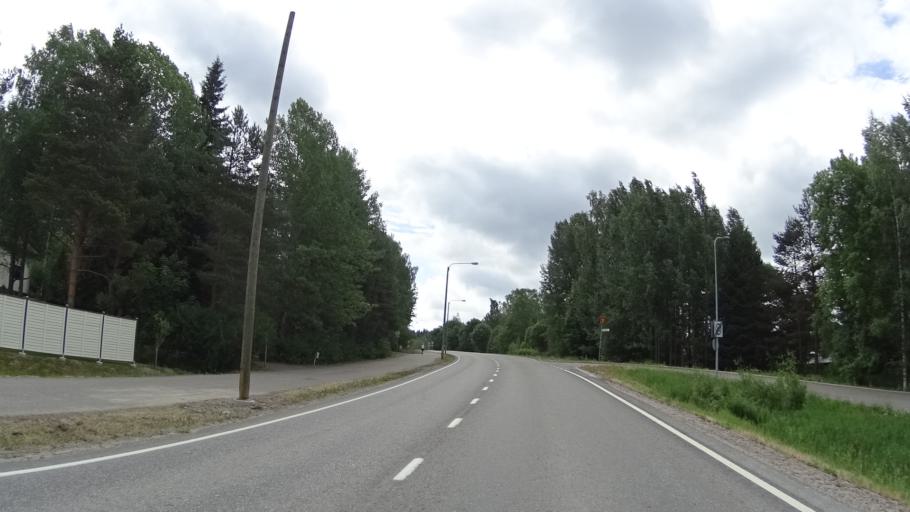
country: FI
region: Uusimaa
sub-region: Helsinki
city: Kirkkonummi
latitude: 60.2736
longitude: 24.4235
